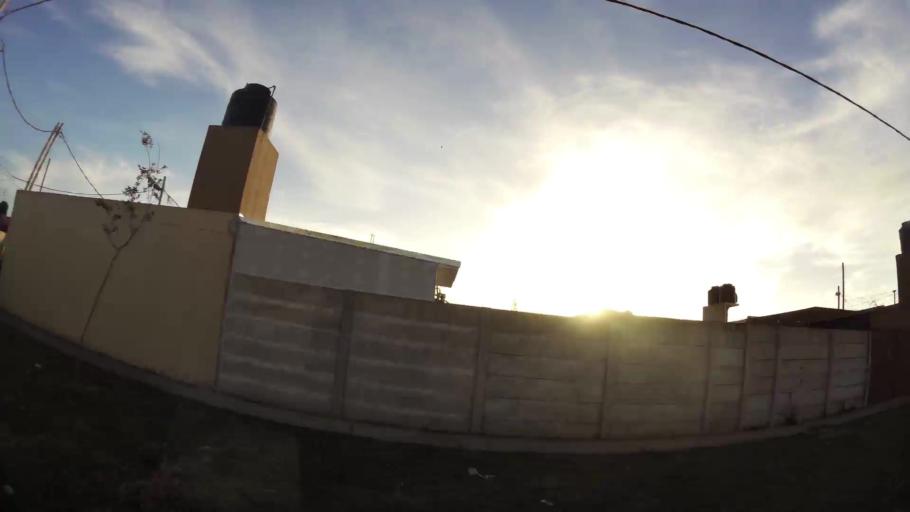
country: AR
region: Buenos Aires
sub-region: Partido de Quilmes
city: Quilmes
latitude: -34.7826
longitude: -58.2193
